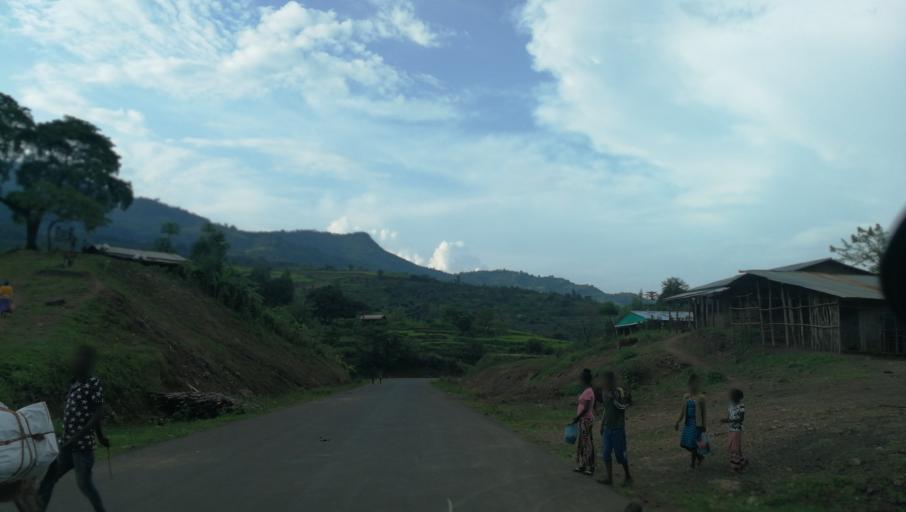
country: ET
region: Southern Nations, Nationalities, and People's Region
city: Areka
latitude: 6.8626
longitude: 37.2620
